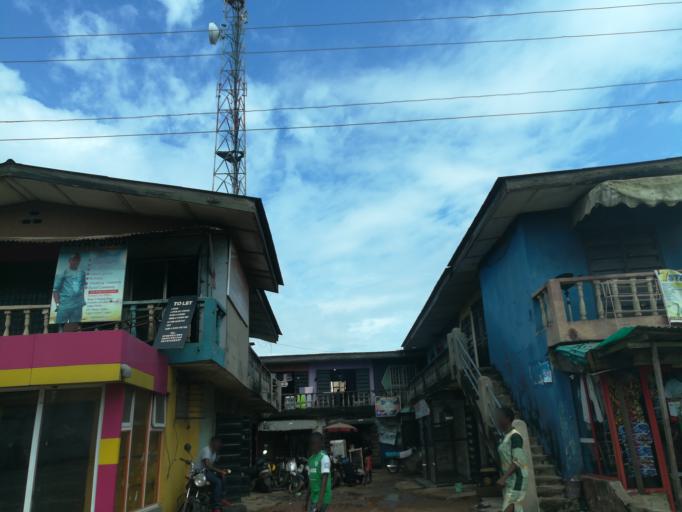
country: NG
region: Lagos
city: Ikorodu
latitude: 6.6121
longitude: 3.5118
